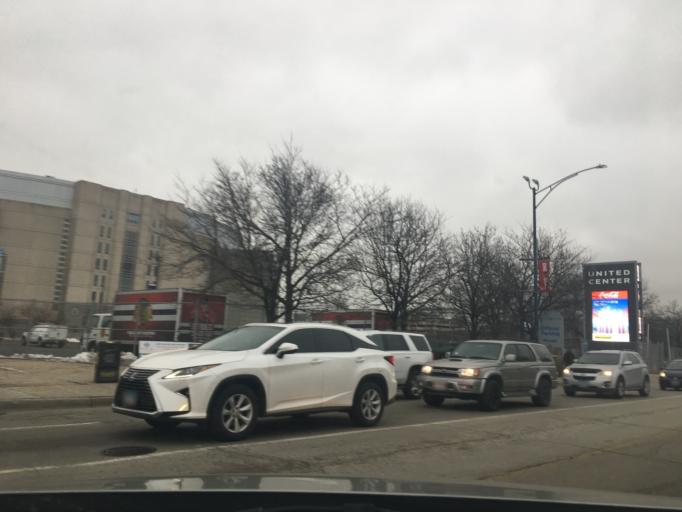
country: US
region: Illinois
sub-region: Cook County
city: Chicago
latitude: 41.8813
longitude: -87.6768
